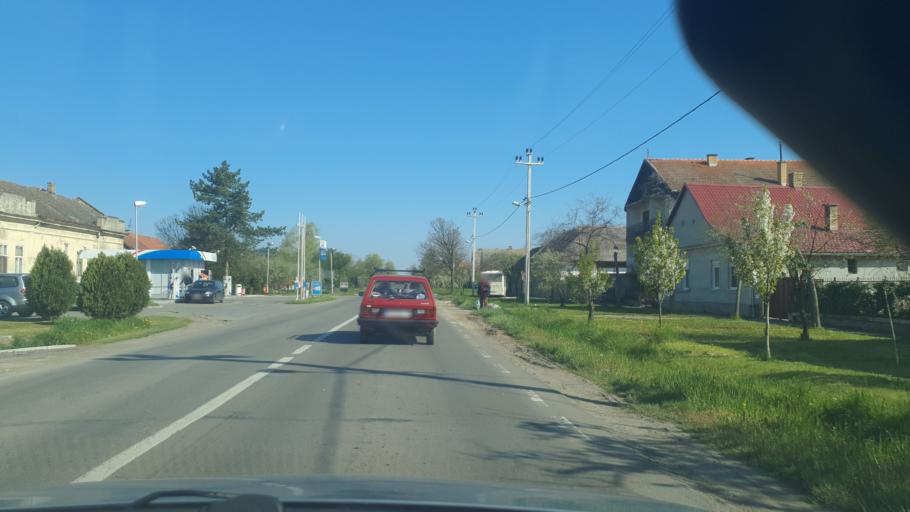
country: RS
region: Autonomna Pokrajina Vojvodina
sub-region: Zapadnobacki Okrug
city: Kula
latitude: 45.7065
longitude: 19.3810
